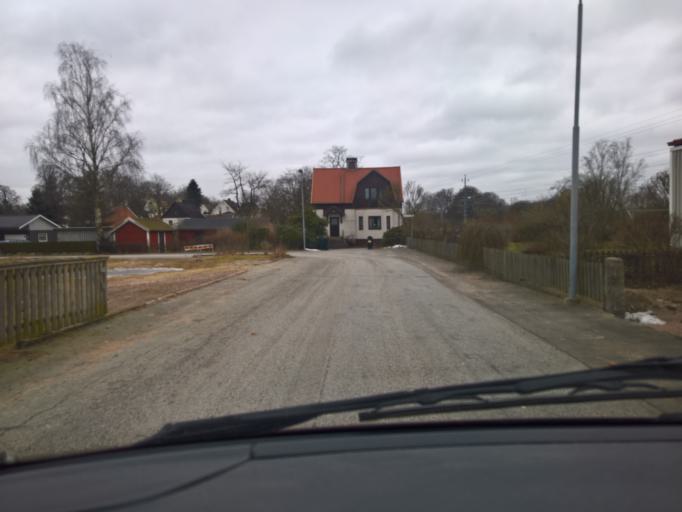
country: SE
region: Skane
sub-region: Hoors Kommun
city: Hoeoer
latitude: 55.9331
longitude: 13.5339
